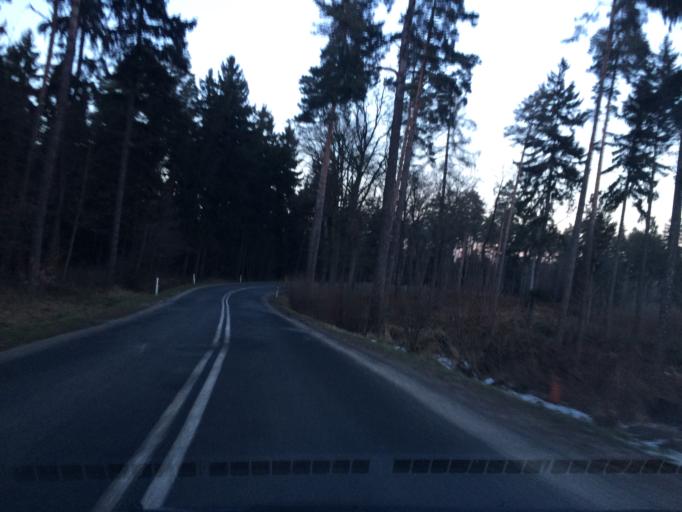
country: PL
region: Lower Silesian Voivodeship
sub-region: Powiat zlotoryjski
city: Olszanica
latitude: 51.1218
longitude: 15.7229
